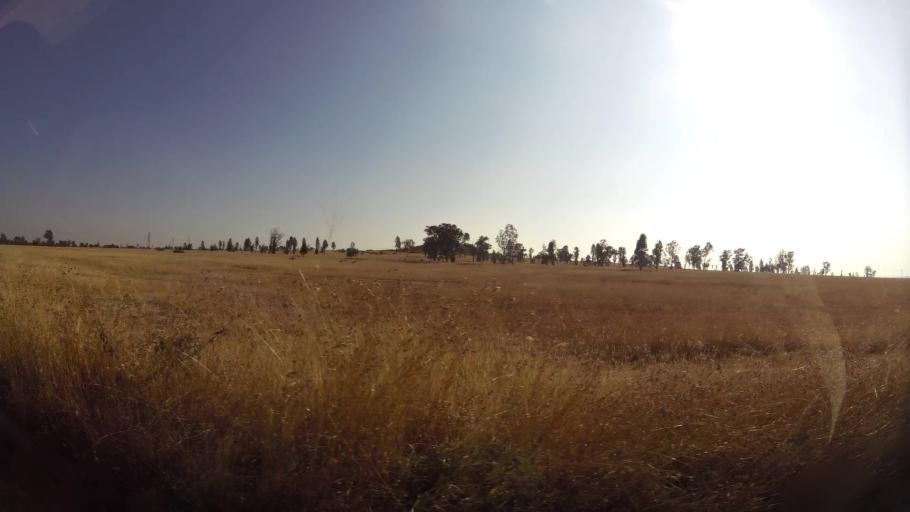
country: ZA
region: Orange Free State
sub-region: Mangaung Metropolitan Municipality
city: Bloemfontein
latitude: -29.1726
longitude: 26.2046
